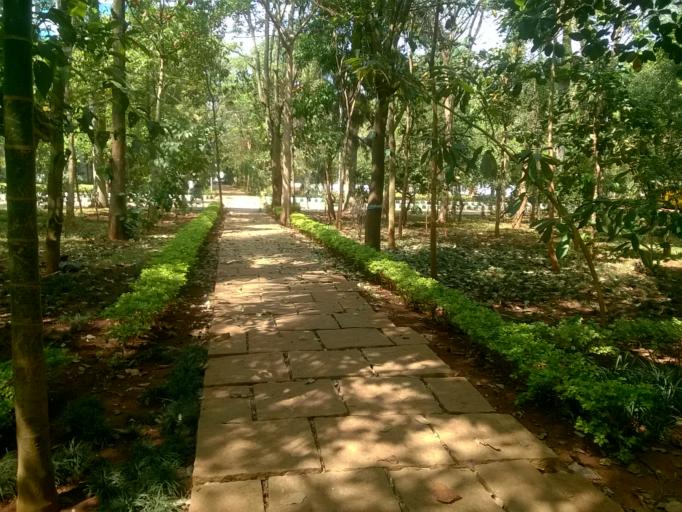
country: IN
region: Karnataka
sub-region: Bangalore Urban
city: Yelahanka
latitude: 13.1328
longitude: 77.5684
